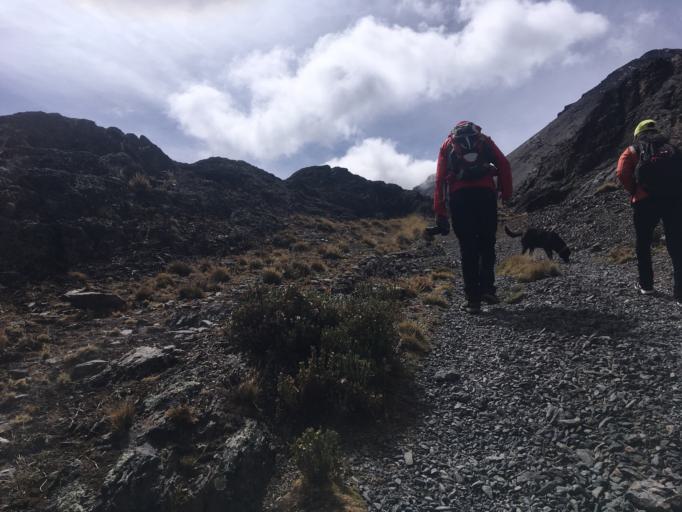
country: BO
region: La Paz
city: La Paz
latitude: -16.3954
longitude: -67.9718
